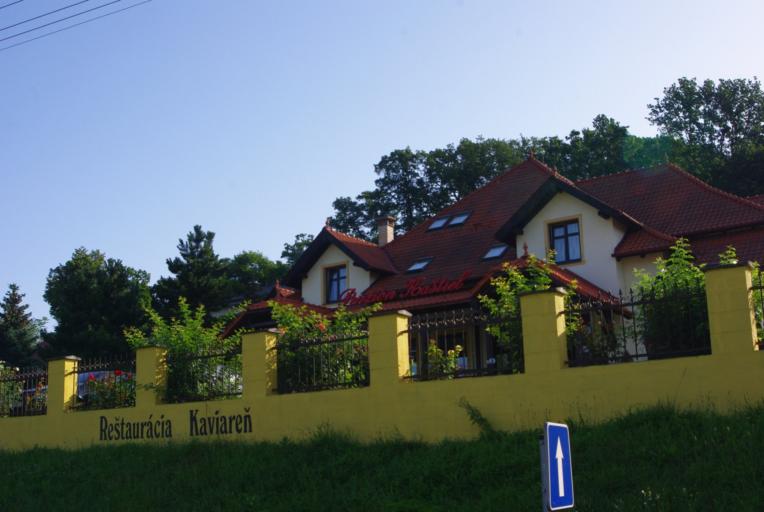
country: SK
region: Banskobystricky
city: Velky Krtis
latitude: 48.2093
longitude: 19.3417
